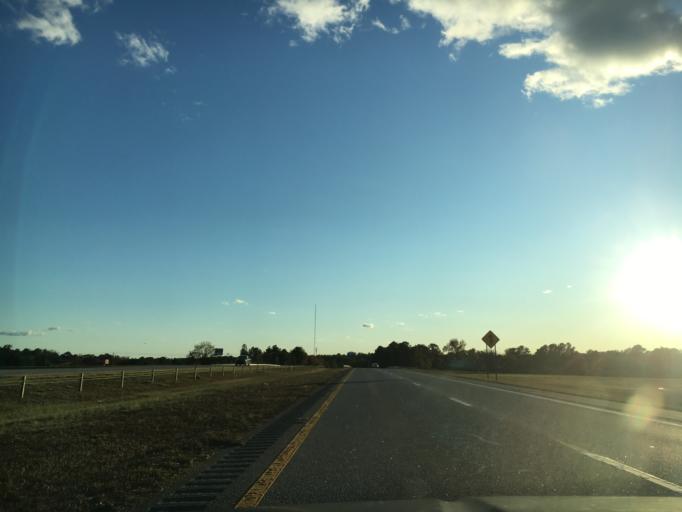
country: US
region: South Carolina
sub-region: Richland County
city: Dentsville
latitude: 34.0582
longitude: -80.9897
